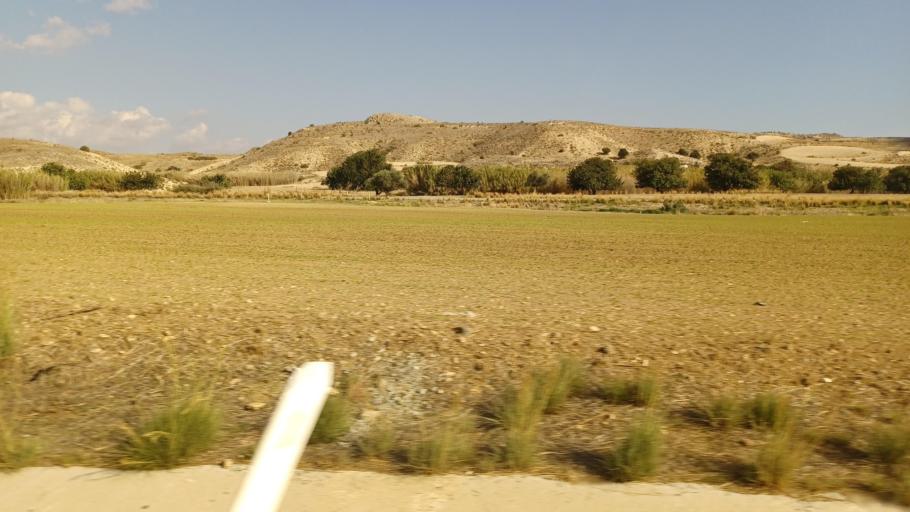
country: CY
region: Larnaka
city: Voroklini
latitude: 34.9954
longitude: 33.6268
